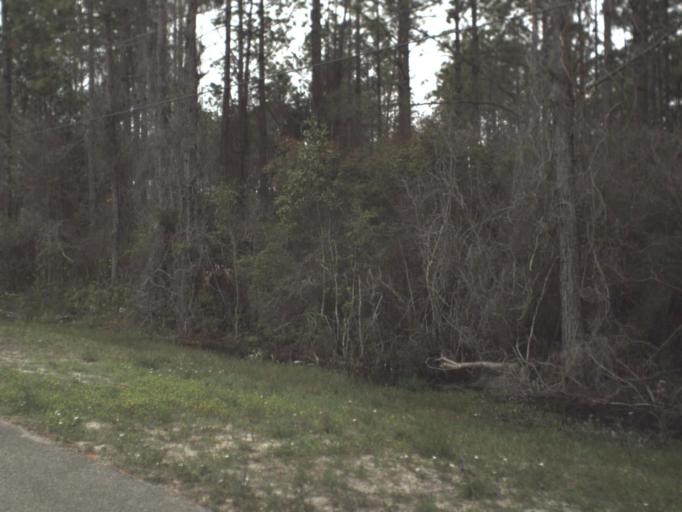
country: US
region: Florida
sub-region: Gulf County
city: Port Saint Joe
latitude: 29.8314
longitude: -85.2770
